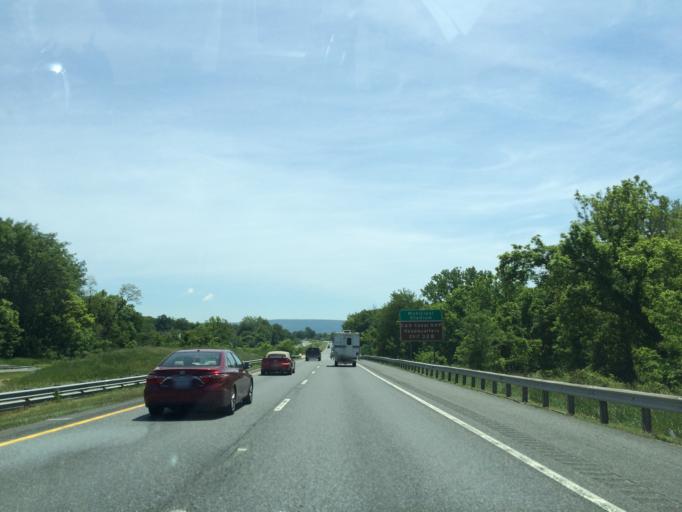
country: US
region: Maryland
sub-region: Washington County
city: Hagerstown
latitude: 39.6033
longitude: -77.7140
